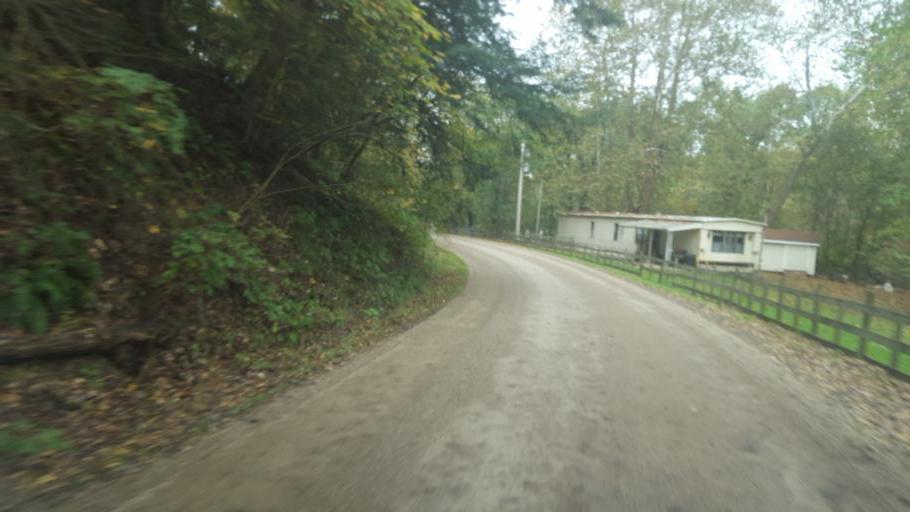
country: US
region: Ohio
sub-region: Ashland County
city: Loudonville
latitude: 40.6074
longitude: -82.2538
